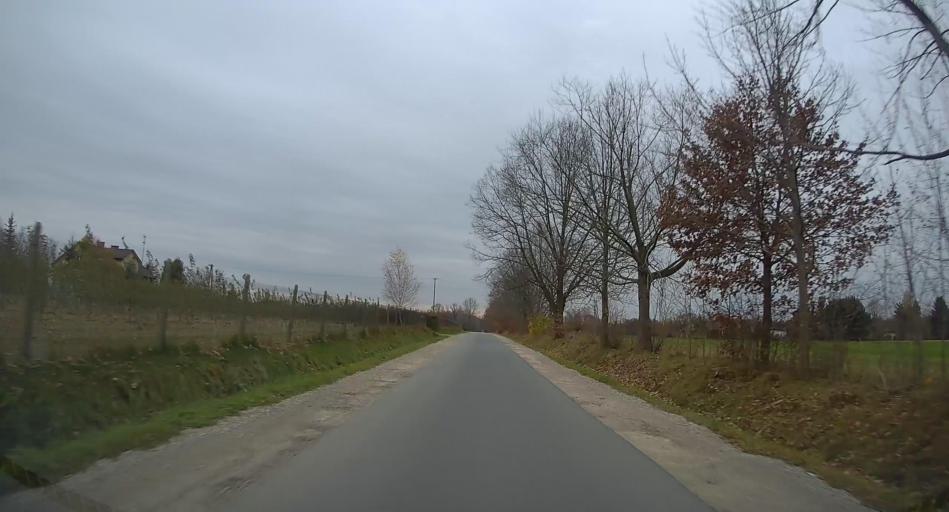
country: PL
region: Lodz Voivodeship
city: Zabia Wola
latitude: 52.0058
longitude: 20.6567
